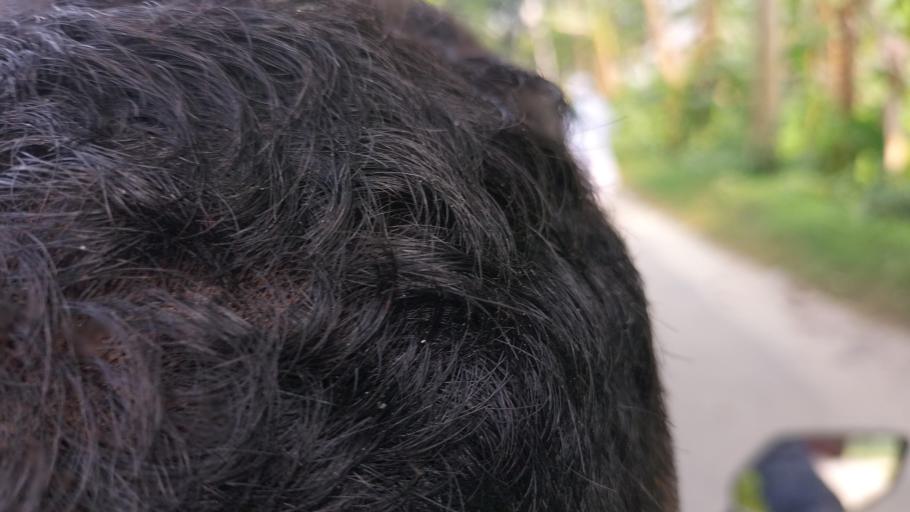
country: BD
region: Dhaka
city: Azimpur
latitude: 23.6912
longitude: 90.2999
